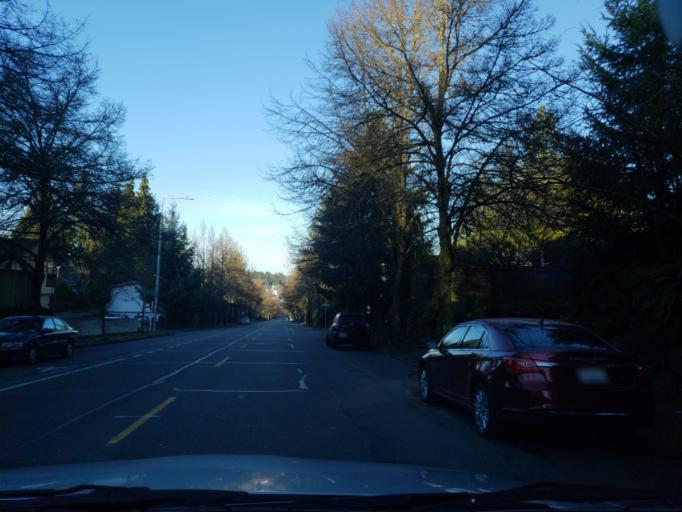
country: US
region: Washington
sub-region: King County
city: Shoreline
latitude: 47.7017
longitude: -122.3177
